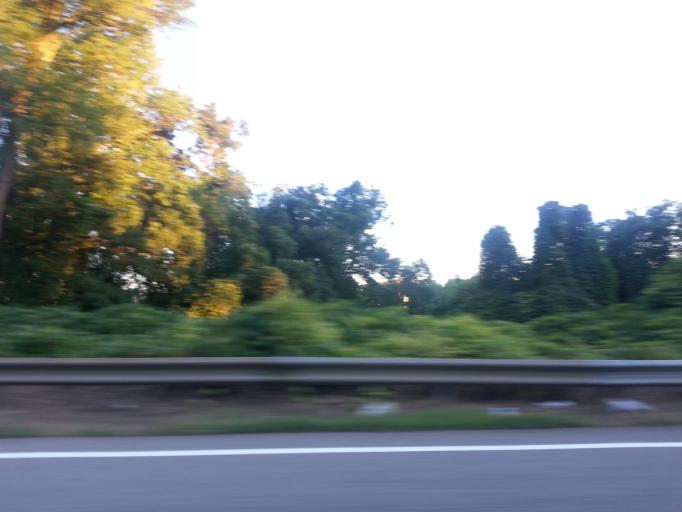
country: US
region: Tennessee
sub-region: Knox County
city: Knoxville
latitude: 35.9655
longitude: -83.8941
